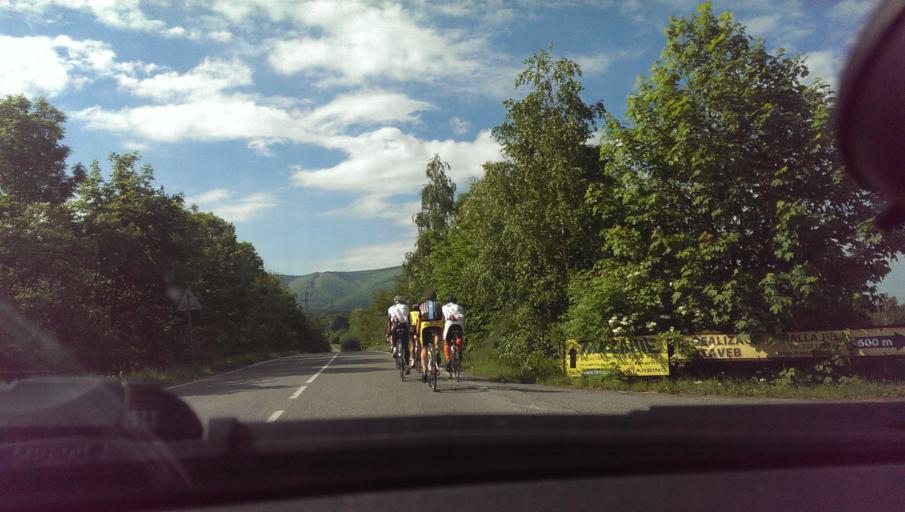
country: CZ
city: Kuncice pod Ondrejnikem
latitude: 49.5375
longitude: 18.2493
